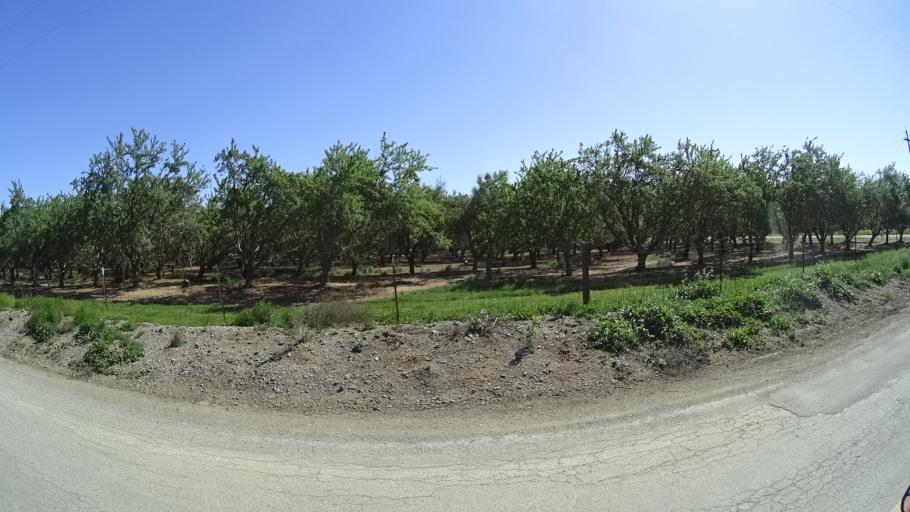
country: US
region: California
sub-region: Glenn County
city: Orland
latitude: 39.6913
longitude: -122.2716
